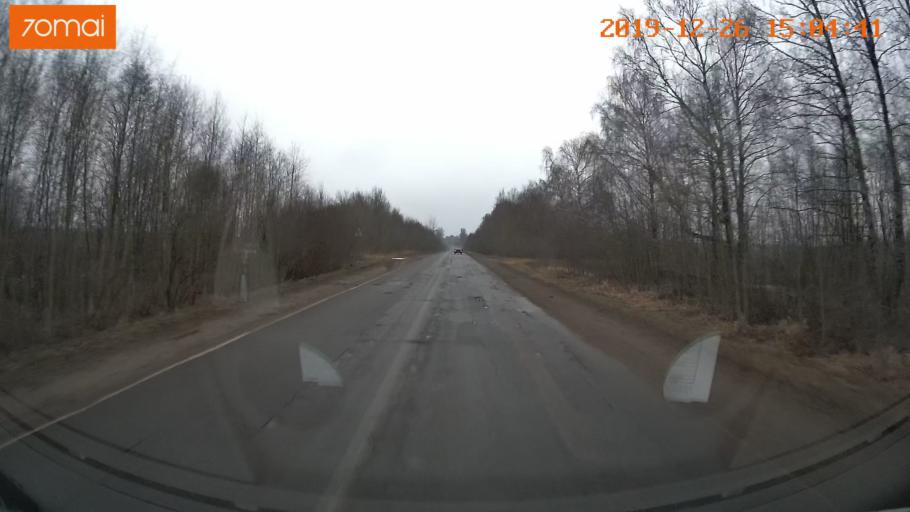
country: RU
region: Jaroslavl
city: Rybinsk
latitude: 58.1972
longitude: 38.8592
